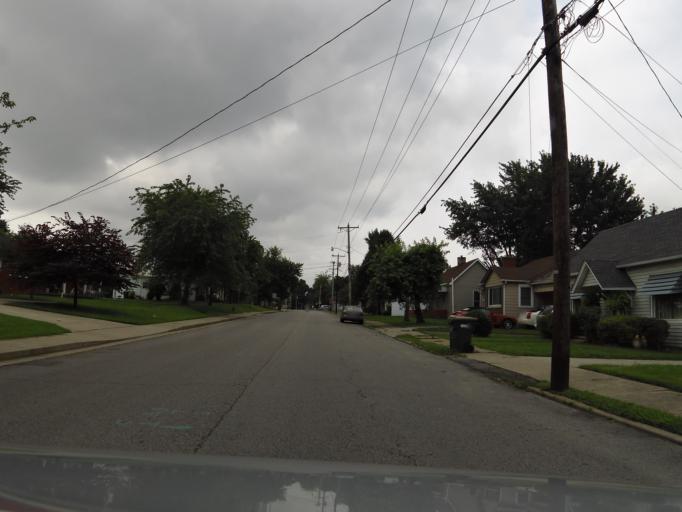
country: US
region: Kentucky
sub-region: Hopkins County
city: Madisonville
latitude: 37.3369
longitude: -87.4991
